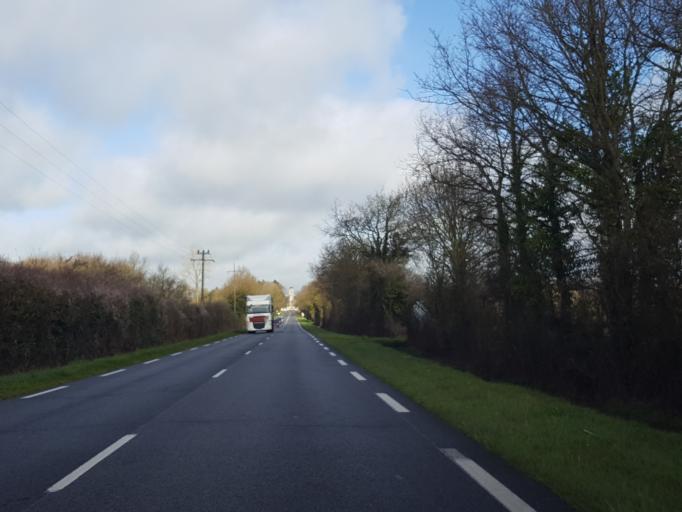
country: FR
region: Pays de la Loire
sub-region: Departement de la Vendee
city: Les Lucs-sur-Boulogne
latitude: 46.8333
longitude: -1.4838
